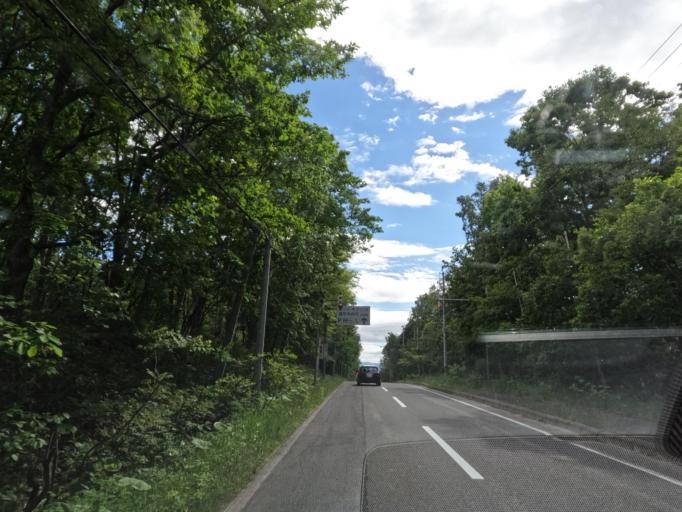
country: JP
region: Hokkaido
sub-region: Asahikawa-shi
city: Asahikawa
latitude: 43.8341
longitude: 142.5352
